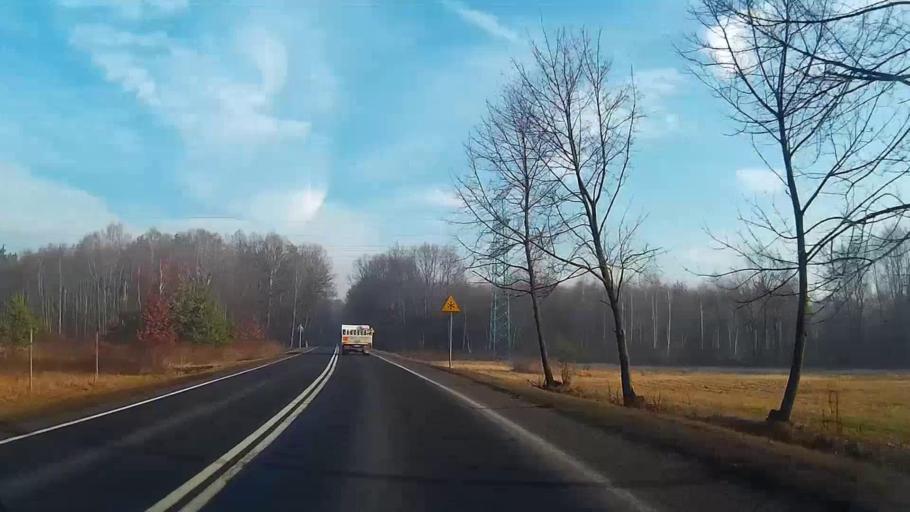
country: PL
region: Lesser Poland Voivodeship
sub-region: Powiat oswiecimski
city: Chelmek
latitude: 50.0728
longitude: 19.2618
